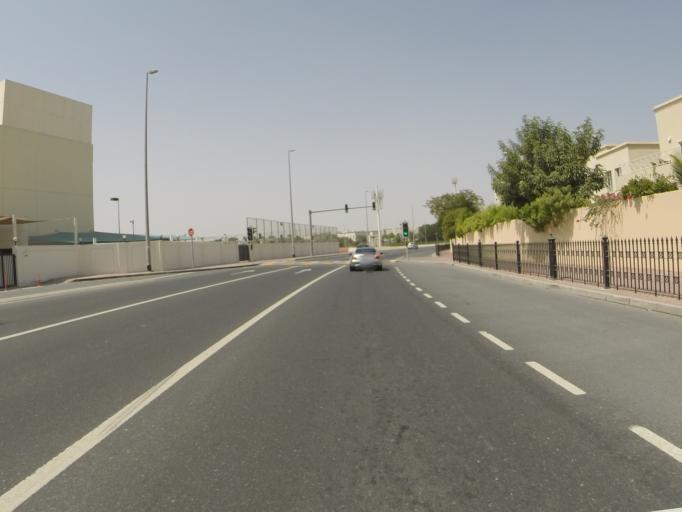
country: AE
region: Dubai
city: Dubai
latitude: 25.0785
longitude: 55.1782
